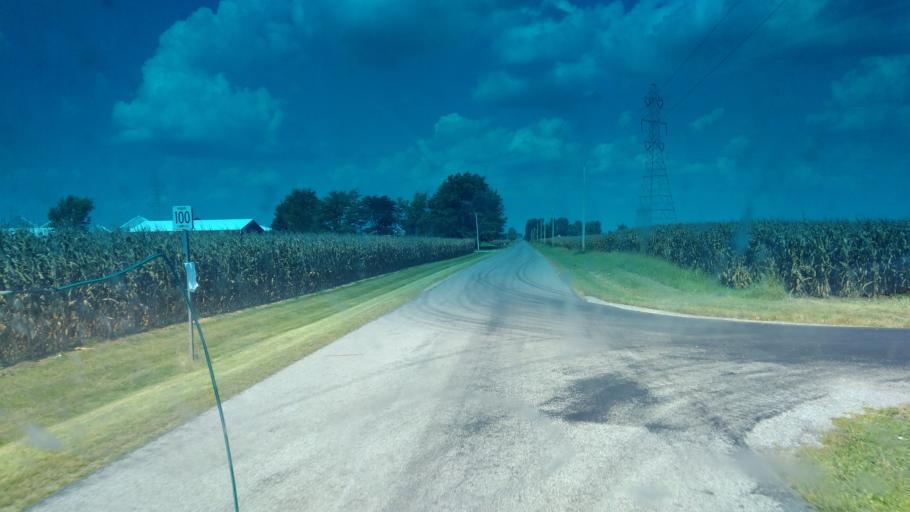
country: US
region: Ohio
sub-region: Hardin County
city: Ada
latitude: 40.6891
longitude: -83.8800
